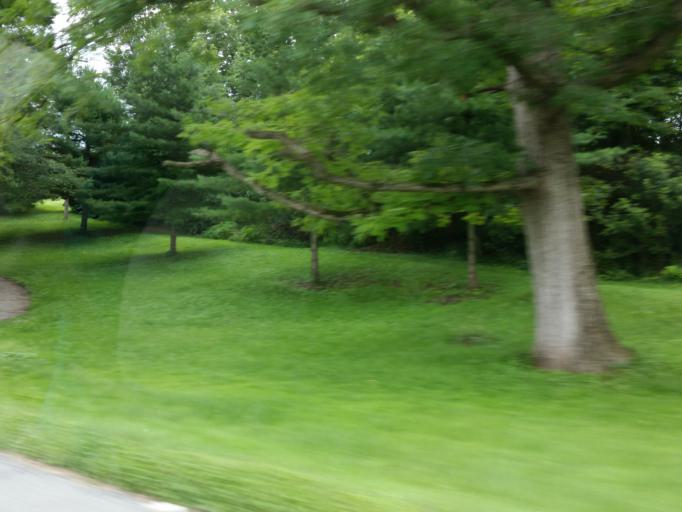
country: US
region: Pennsylvania
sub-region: York County
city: North York
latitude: 40.0004
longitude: -76.7486
